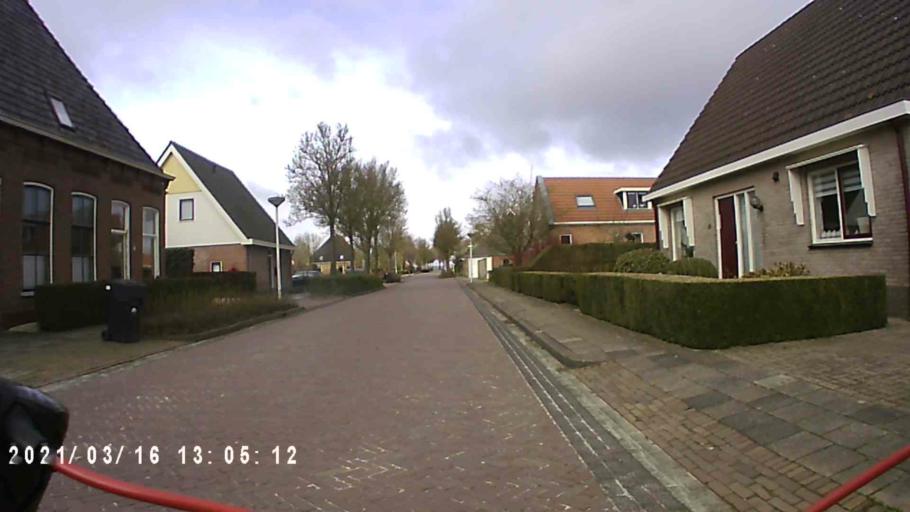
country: NL
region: Friesland
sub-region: Menameradiel
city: Berltsum
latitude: 53.2517
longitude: 5.6286
